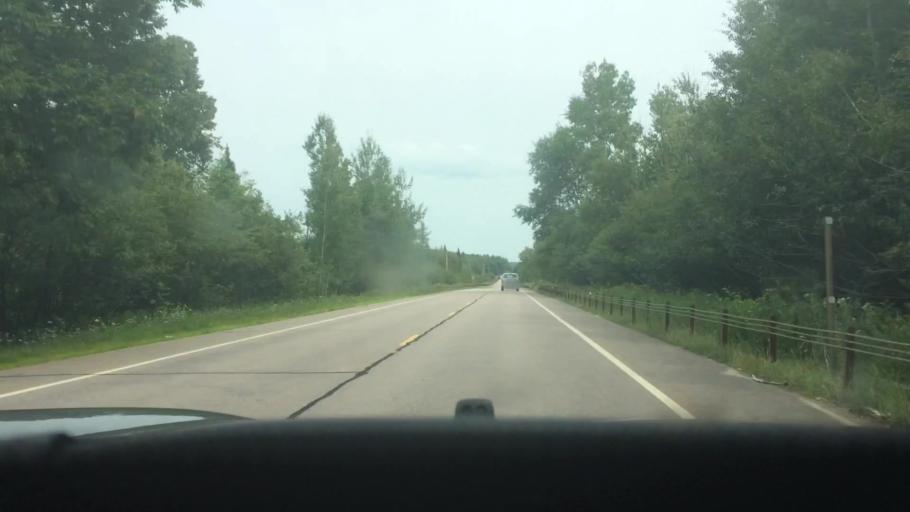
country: US
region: New York
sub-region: Franklin County
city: Malone
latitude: 44.8549
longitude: -74.0635
